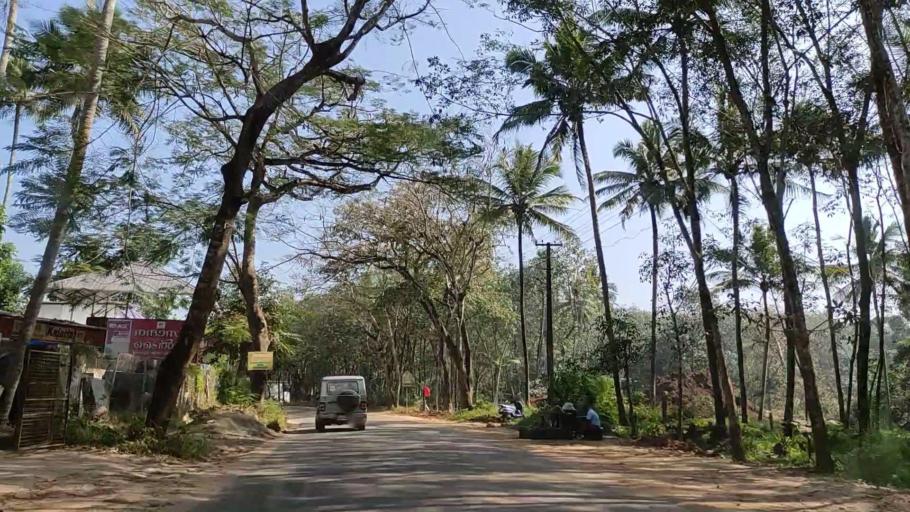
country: IN
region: Kerala
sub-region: Kollam
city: Punalur
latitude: 8.9081
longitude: 76.8774
